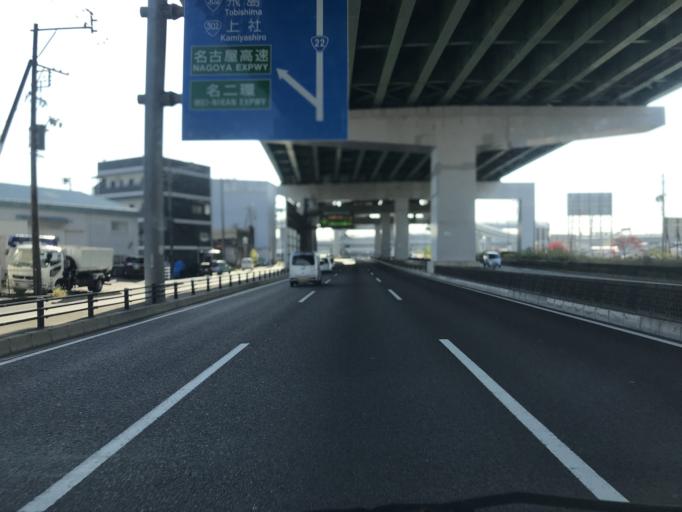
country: JP
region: Aichi
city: Iwakura
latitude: 35.2254
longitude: 136.8535
